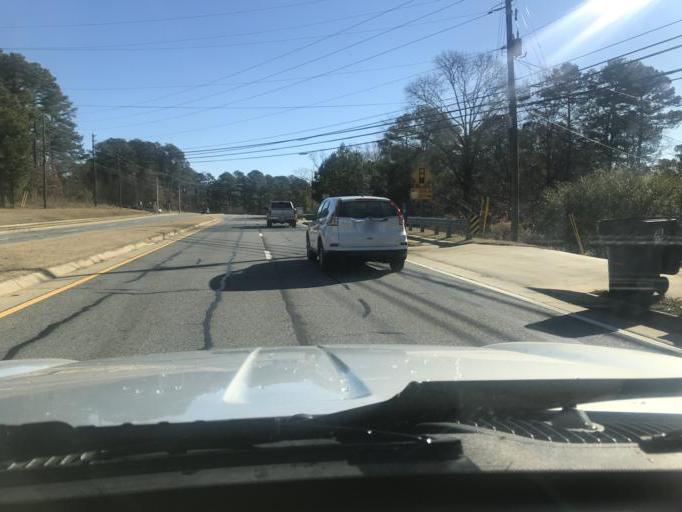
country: US
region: Georgia
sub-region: Gwinnett County
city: Lawrenceville
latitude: 33.9725
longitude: -84.0525
